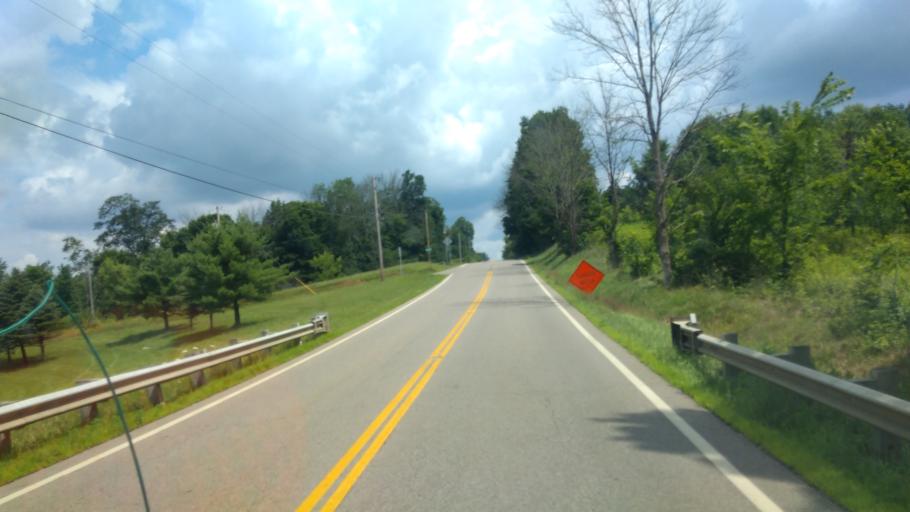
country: US
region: Ohio
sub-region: Ashland County
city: Loudonville
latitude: 40.7060
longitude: -82.3180
